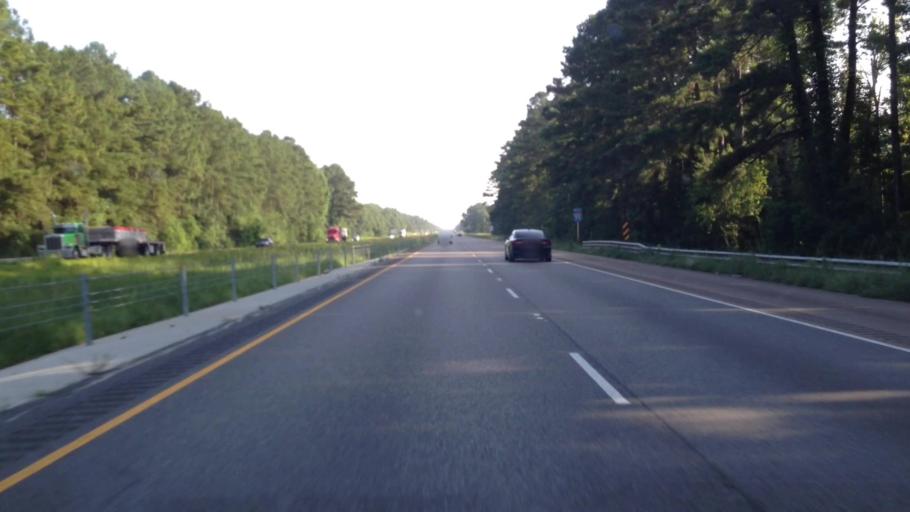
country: US
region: Louisiana
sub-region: Tangipahoa Parish
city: Natalbany
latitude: 30.5269
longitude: -90.5038
